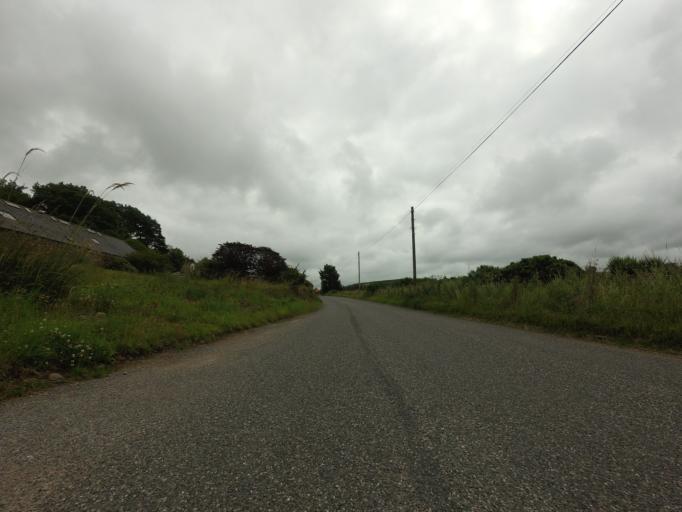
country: GB
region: Scotland
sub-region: Aberdeenshire
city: Turriff
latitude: 57.5331
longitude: -2.3820
